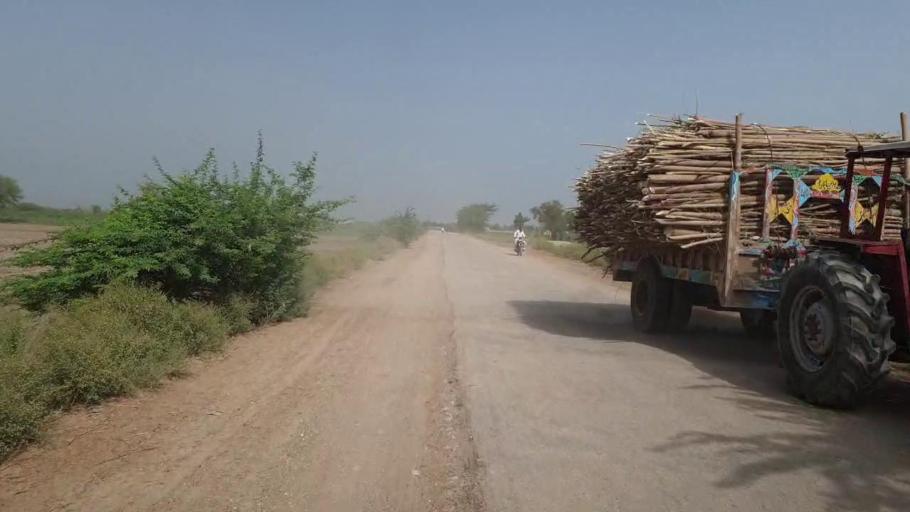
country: PK
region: Sindh
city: Daulatpur
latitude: 26.5495
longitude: 68.0590
